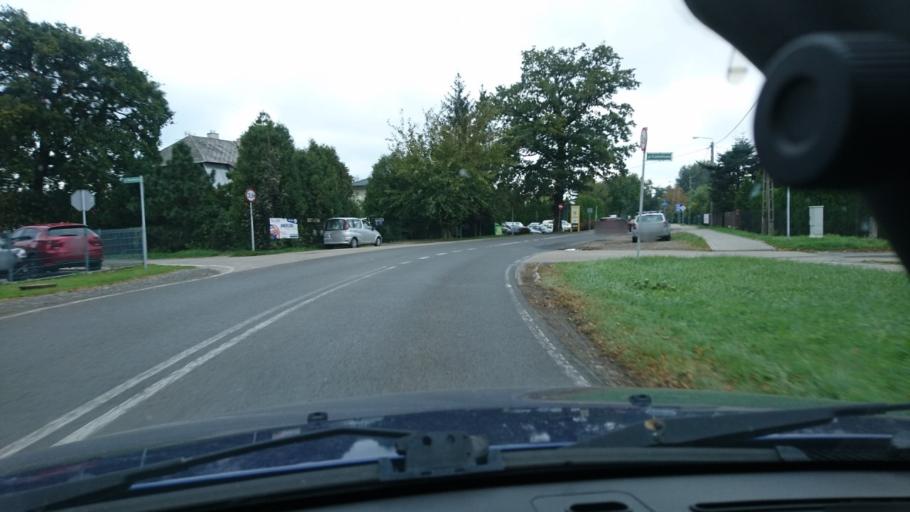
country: PL
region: Silesian Voivodeship
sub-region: Powiat bielski
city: Jaworze
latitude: 49.8038
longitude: 18.9820
